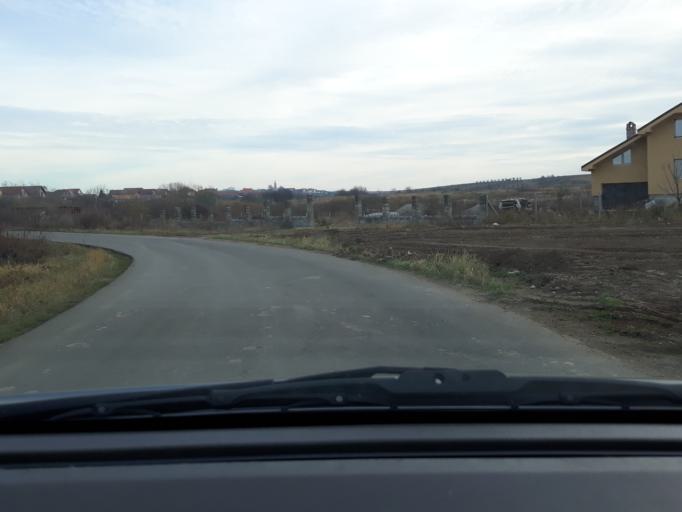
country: RO
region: Bihor
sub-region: Comuna Sanmartin
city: Sanmartin
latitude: 47.0192
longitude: 22.0067
